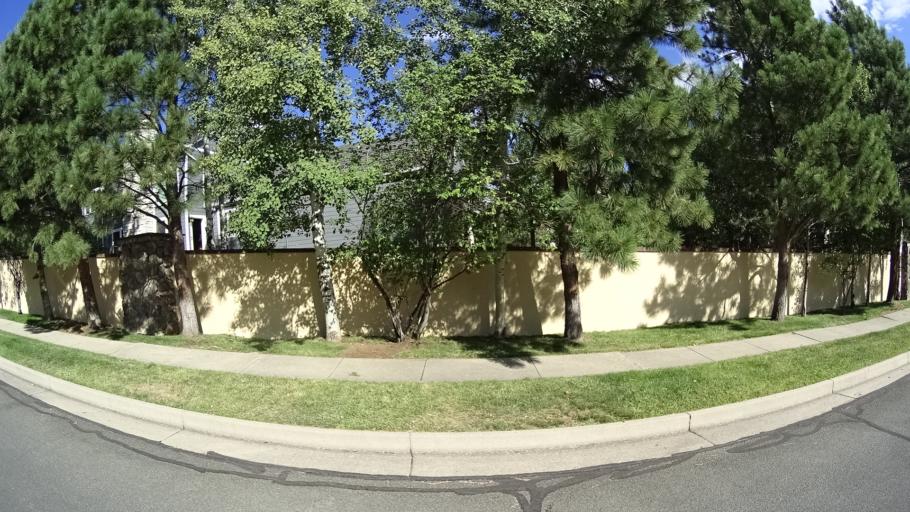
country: US
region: Colorado
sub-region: El Paso County
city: Fort Carson
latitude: 38.7651
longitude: -104.8335
